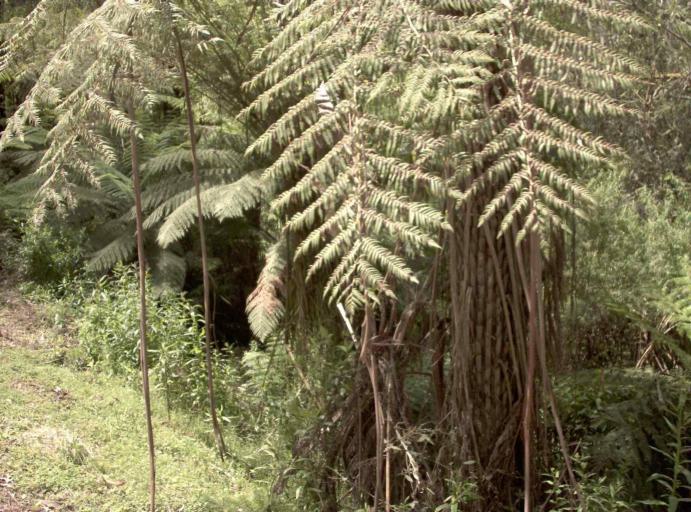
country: AU
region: Victoria
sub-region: Latrobe
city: Traralgon
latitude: -38.4409
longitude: 146.5375
